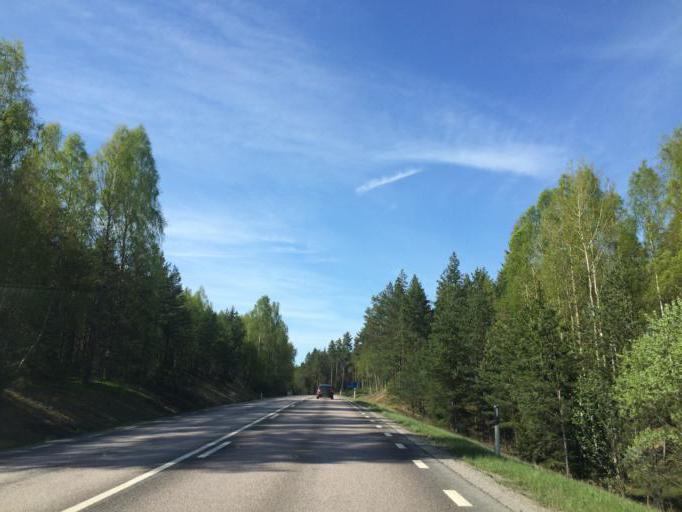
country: SE
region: Soedermanland
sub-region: Katrineholms Kommun
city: Katrineholm
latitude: 59.0949
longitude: 16.1929
